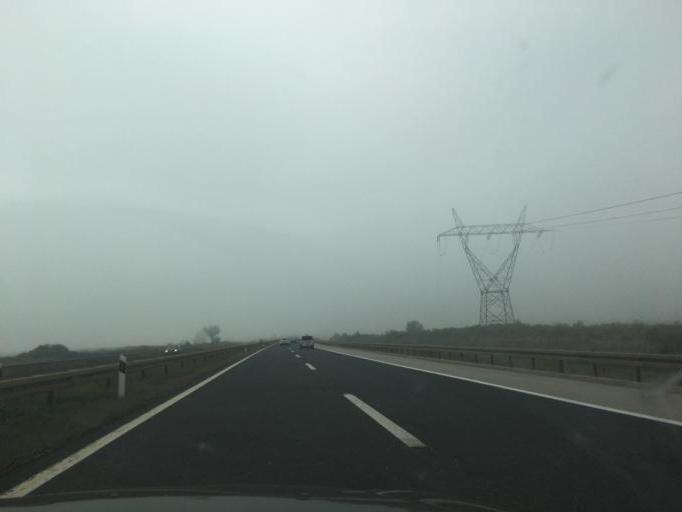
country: HR
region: Licko-Senjska
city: Gospic
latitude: 44.6081
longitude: 15.4400
